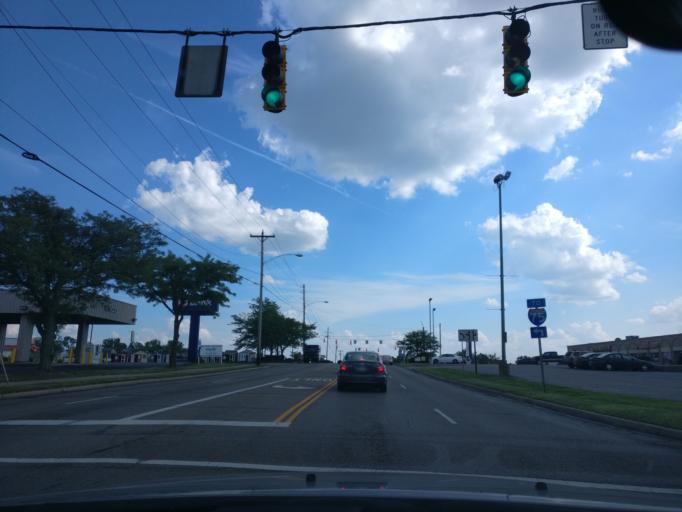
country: US
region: Ohio
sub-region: Montgomery County
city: West Carrollton City
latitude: 39.6421
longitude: -84.2435
